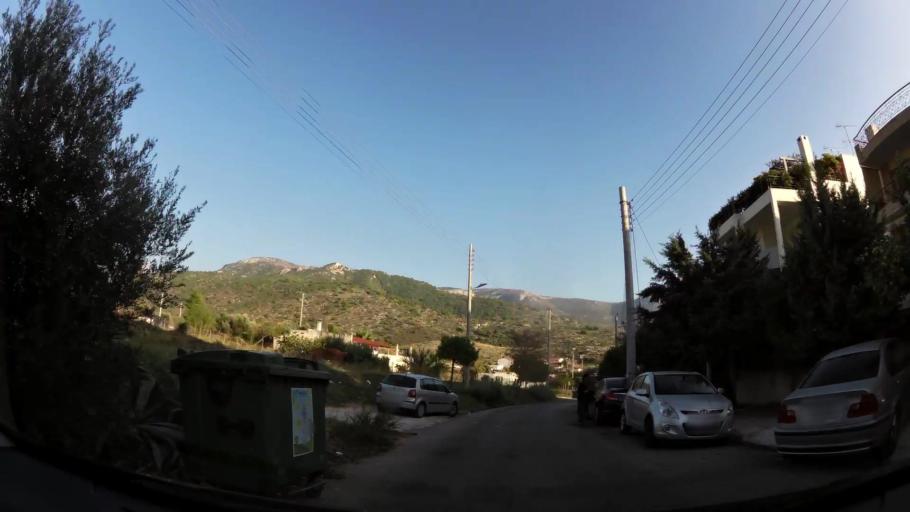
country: GR
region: Attica
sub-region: Nomarchia Athinas
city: Argyroupoli
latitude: 37.9028
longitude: 23.7732
